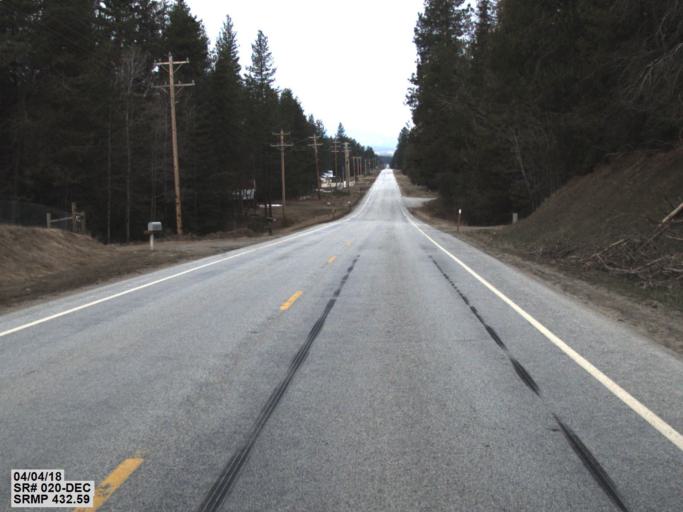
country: US
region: Washington
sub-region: Pend Oreille County
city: Newport
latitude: 48.2213
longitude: -117.1076
